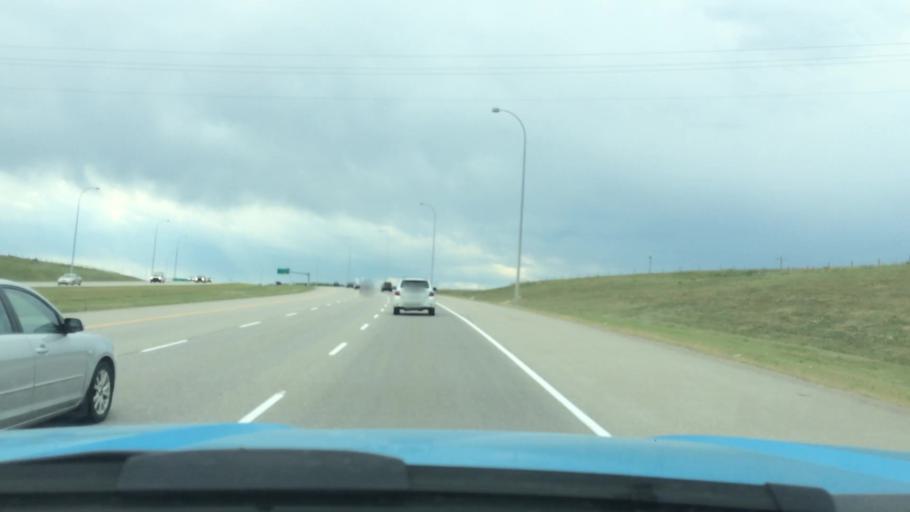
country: CA
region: Alberta
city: Calgary
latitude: 51.1515
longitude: -114.1873
